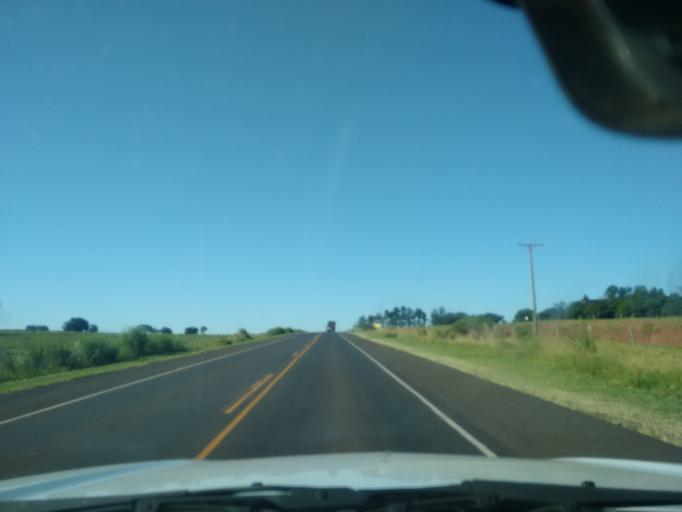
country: PY
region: Canindeyu
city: Salto del Guaira
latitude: -23.9769
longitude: -54.3310
